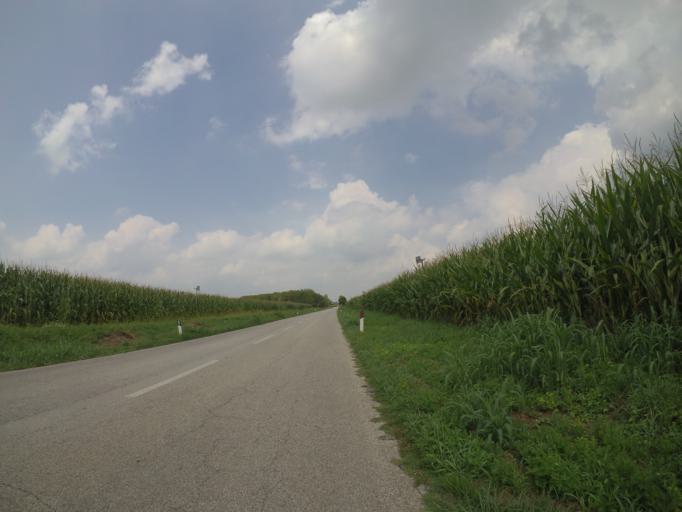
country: IT
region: Friuli Venezia Giulia
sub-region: Provincia di Udine
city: Sedegliano
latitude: 46.0145
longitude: 13.0081
